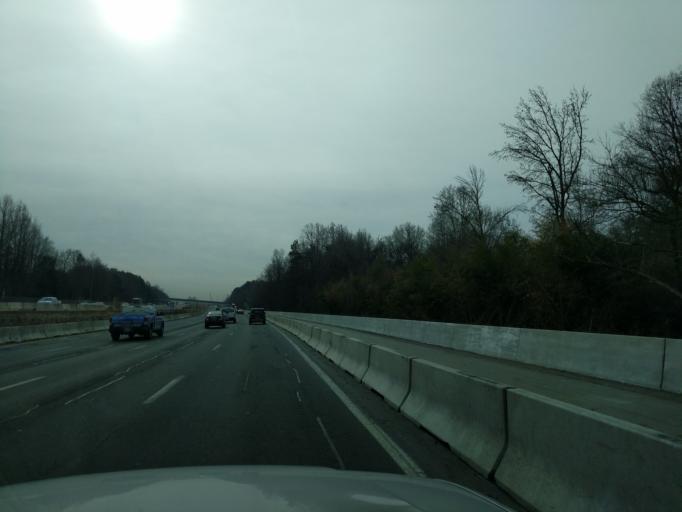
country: US
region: North Carolina
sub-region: Mecklenburg County
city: Charlotte
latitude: 35.2890
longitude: -80.8509
